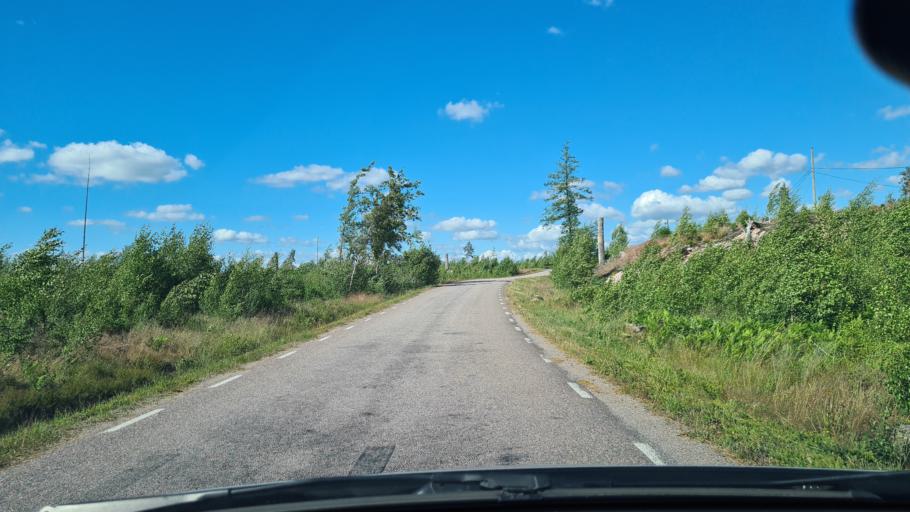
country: SE
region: OEstergoetland
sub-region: Norrkopings Kommun
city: Krokek
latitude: 58.7327
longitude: 16.4680
